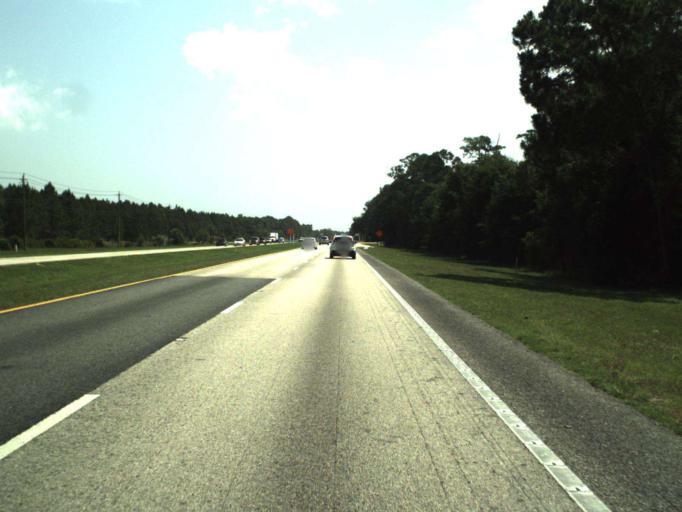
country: US
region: Florida
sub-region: Volusia County
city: Daytona Beach
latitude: 29.1568
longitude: -81.1007
